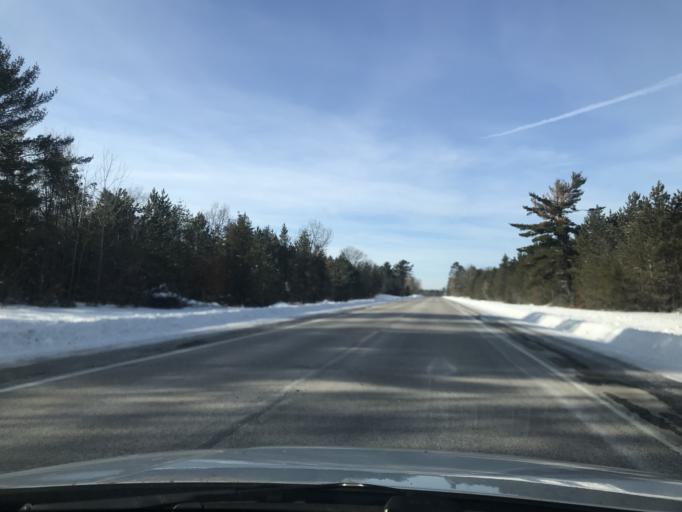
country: US
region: Wisconsin
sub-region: Oconto County
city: Gillett
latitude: 45.1208
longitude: -88.3902
